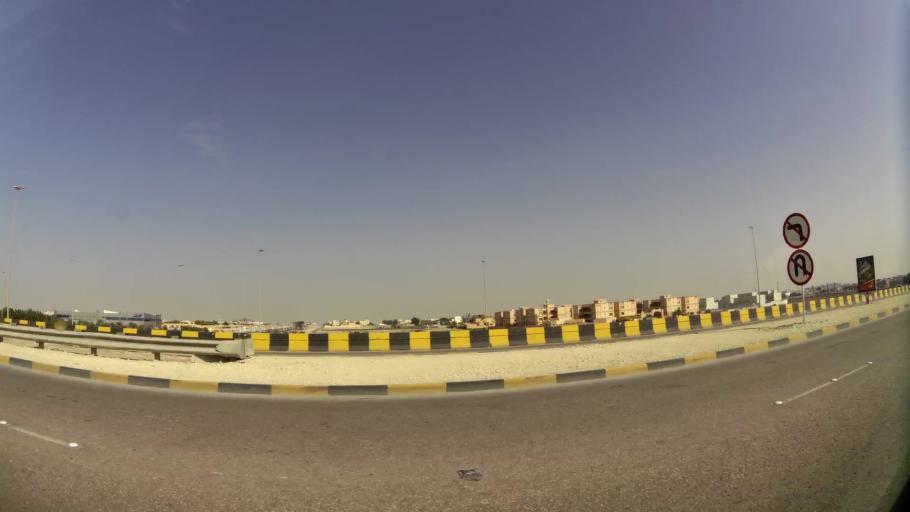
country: BH
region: Central Governorate
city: Madinat Hamad
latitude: 26.1719
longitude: 50.4654
